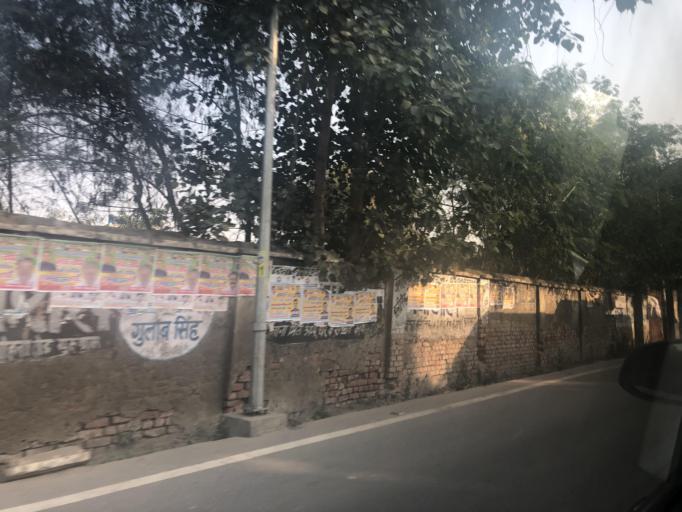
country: IN
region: Haryana
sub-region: Gurgaon
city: Gurgaon
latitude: 28.5634
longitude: 77.0012
